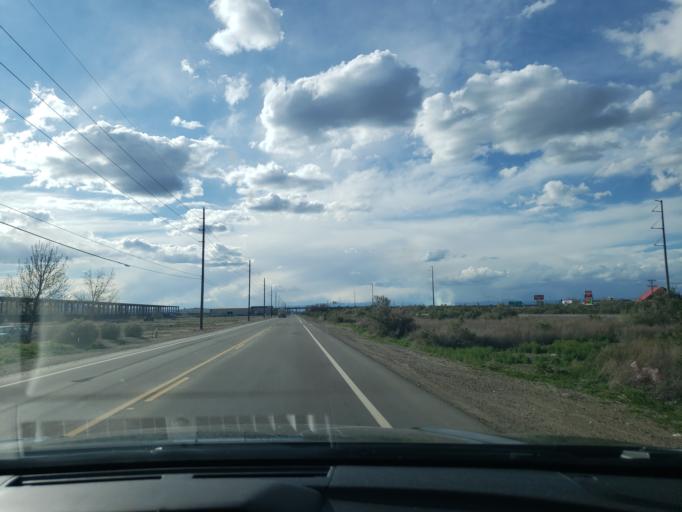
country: US
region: Colorado
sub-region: Mesa County
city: Redlands
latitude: 39.1066
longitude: -108.6396
